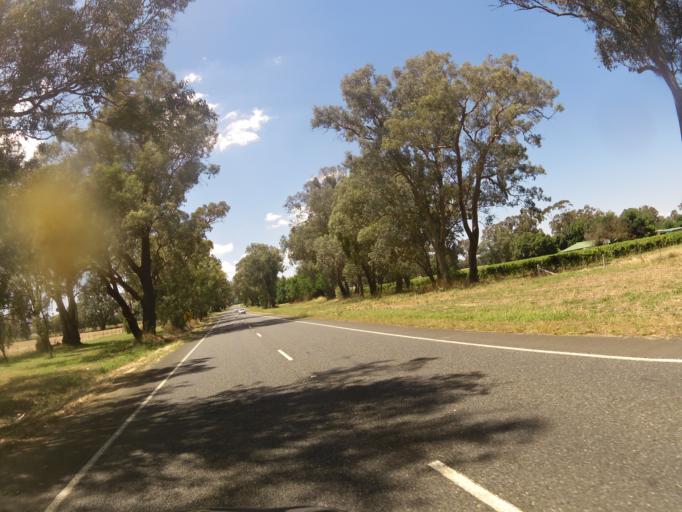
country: AU
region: Victoria
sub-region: Wangaratta
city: Wangaratta
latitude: -36.4319
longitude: 146.5317
